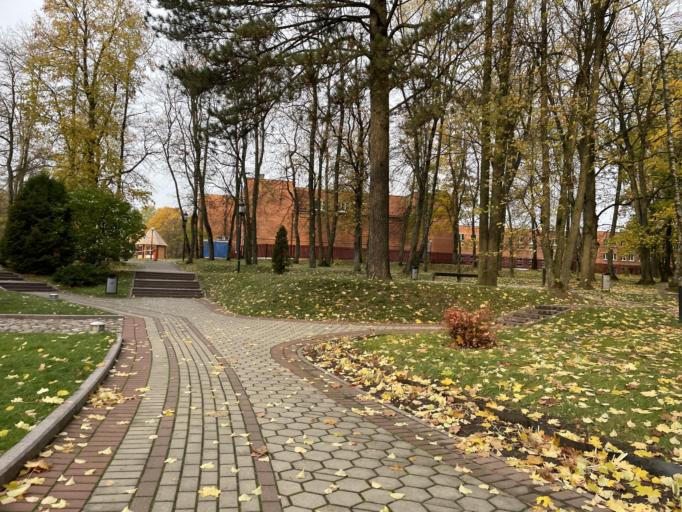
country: BY
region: Grodnenskaya
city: Mir
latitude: 53.4513
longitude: 26.4755
